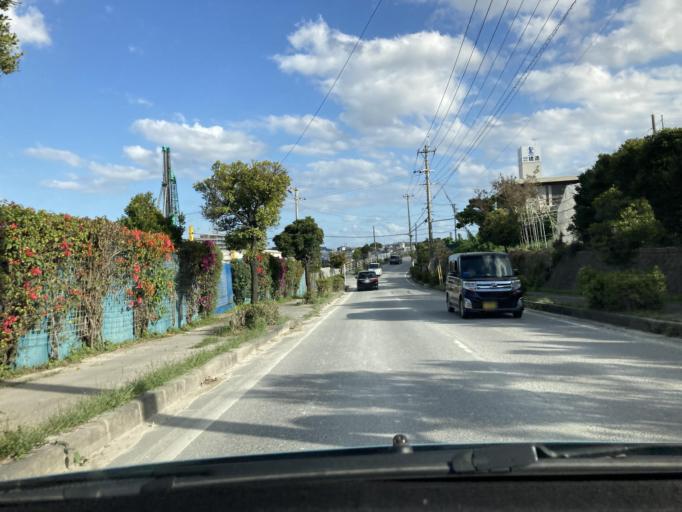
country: JP
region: Okinawa
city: Tomigusuku
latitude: 26.1897
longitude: 127.7049
